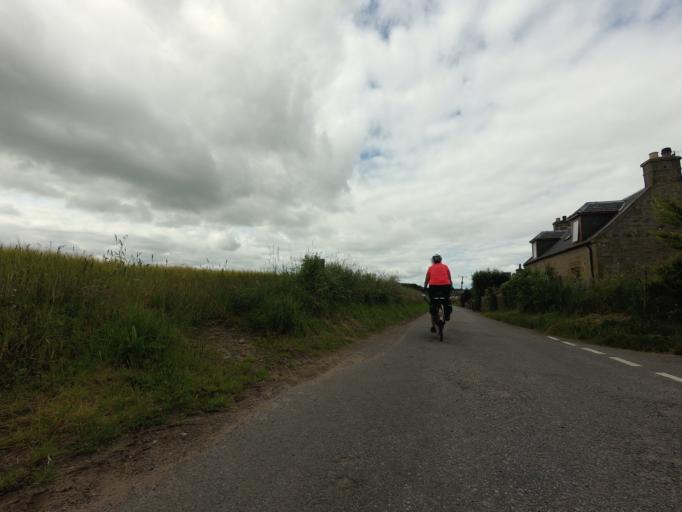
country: GB
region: Scotland
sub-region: Moray
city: Kinloss
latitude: 57.6349
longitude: -3.5180
